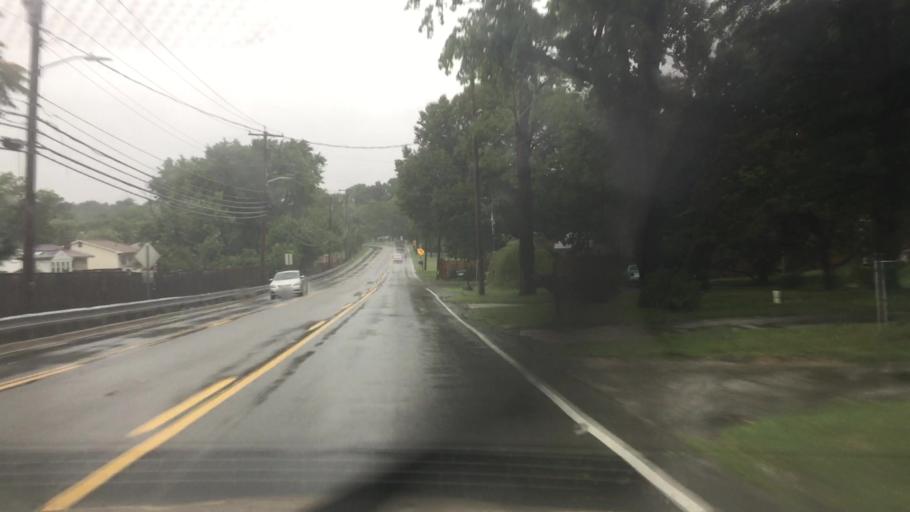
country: US
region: Maryland
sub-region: Anne Arundel County
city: Severn
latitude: 39.1392
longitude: -76.7232
